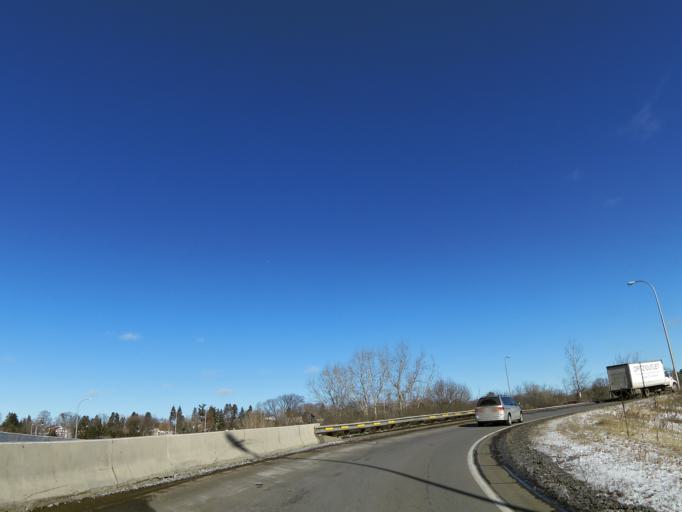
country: US
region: Minnesota
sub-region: Hennepin County
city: Saint Louis Park
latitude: 44.9719
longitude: -93.3425
